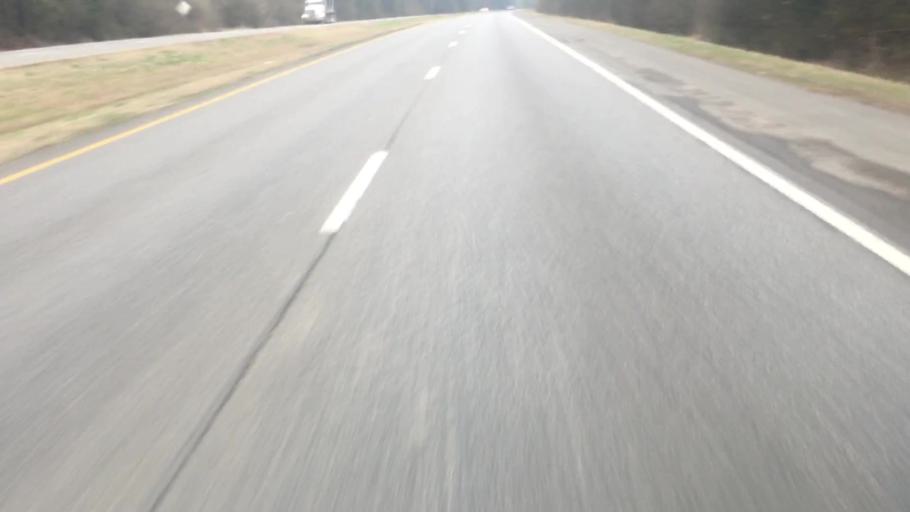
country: US
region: Alabama
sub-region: Jefferson County
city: Graysville
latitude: 33.6763
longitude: -86.9722
